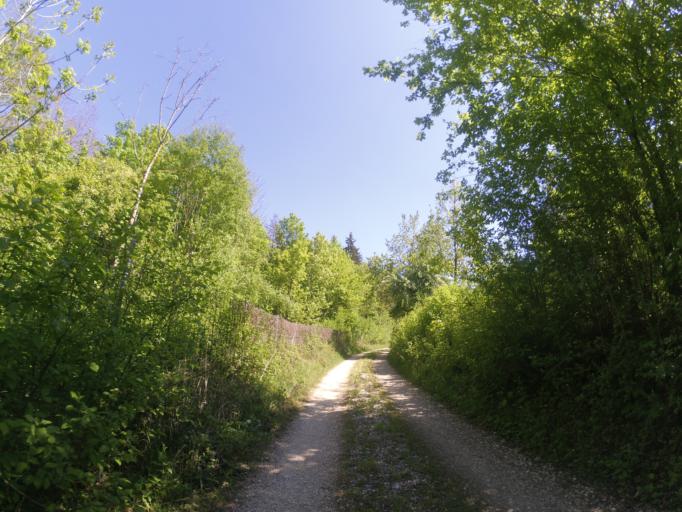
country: DE
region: Baden-Wuerttemberg
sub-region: Tuebingen Region
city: Ulm
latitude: 48.4262
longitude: 9.9637
